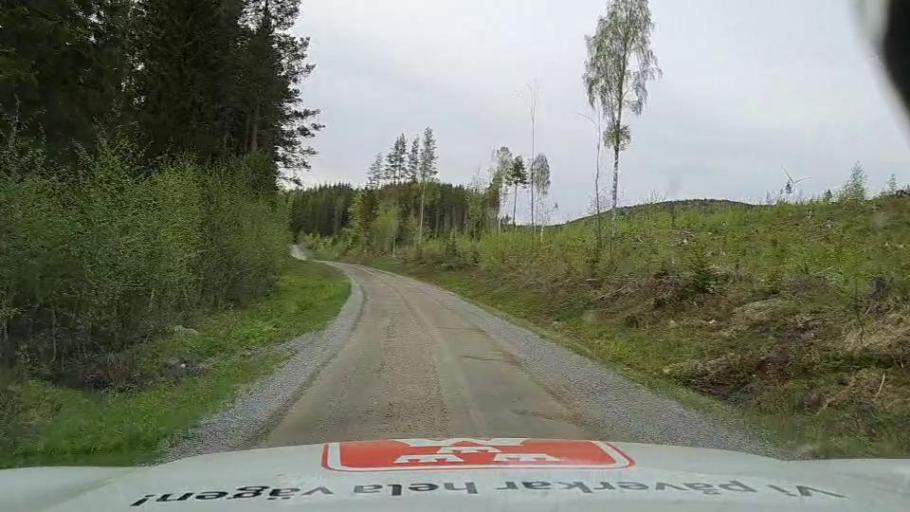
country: SE
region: Jaemtland
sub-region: Bergs Kommun
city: Hoverberg
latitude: 62.5290
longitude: 14.9156
